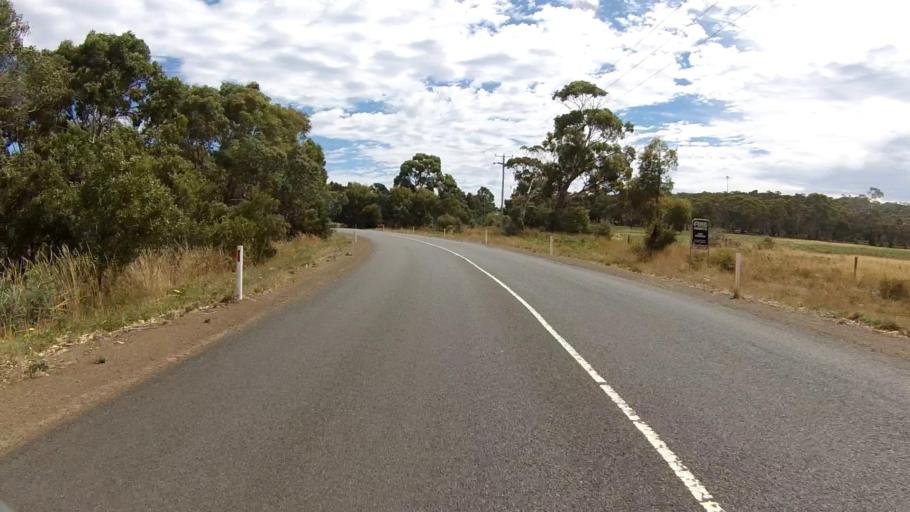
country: AU
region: Tasmania
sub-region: Sorell
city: Sorell
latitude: -42.8851
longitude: 147.6688
